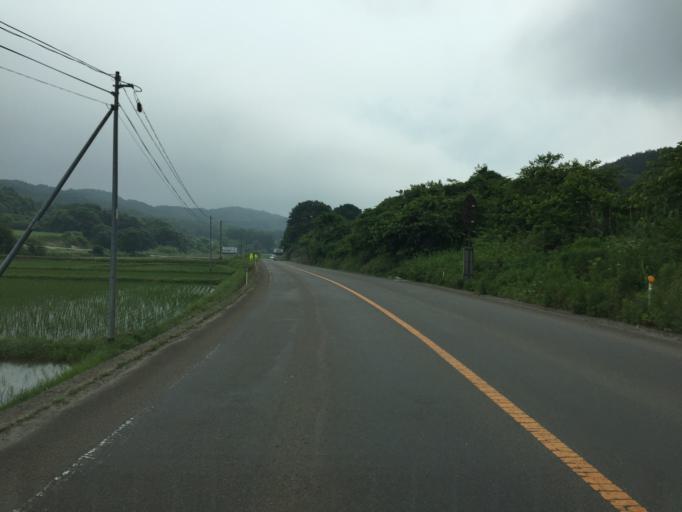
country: JP
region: Fukushima
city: Yanagawamachi-saiwaicho
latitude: 37.7622
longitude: 140.7302
